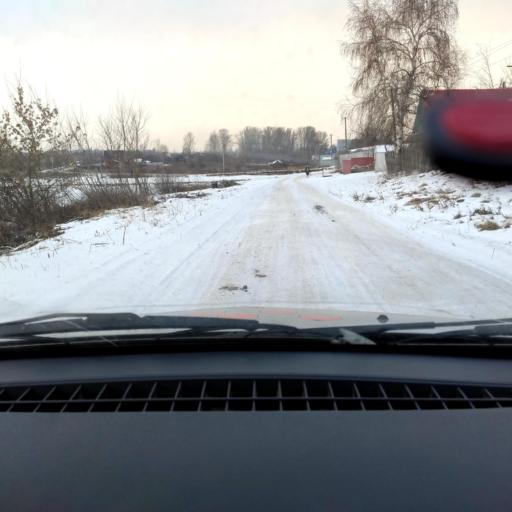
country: RU
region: Bashkortostan
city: Blagoveshchensk
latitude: 54.8879
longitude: 56.0390
